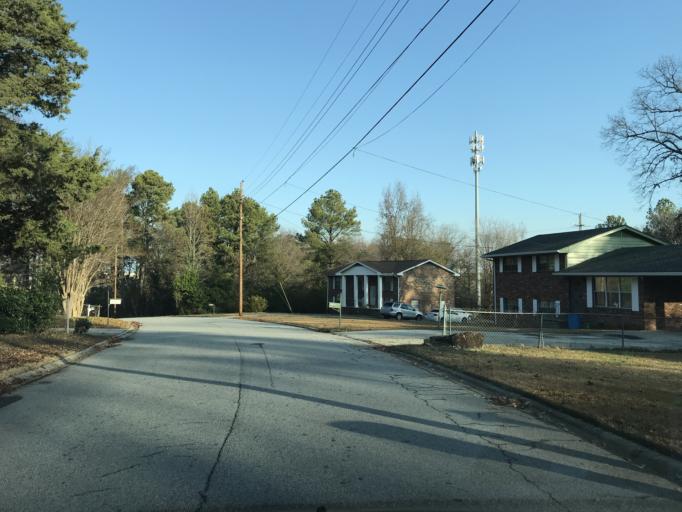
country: US
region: Georgia
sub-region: Clayton County
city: Riverdale
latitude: 33.6139
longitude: -84.4294
